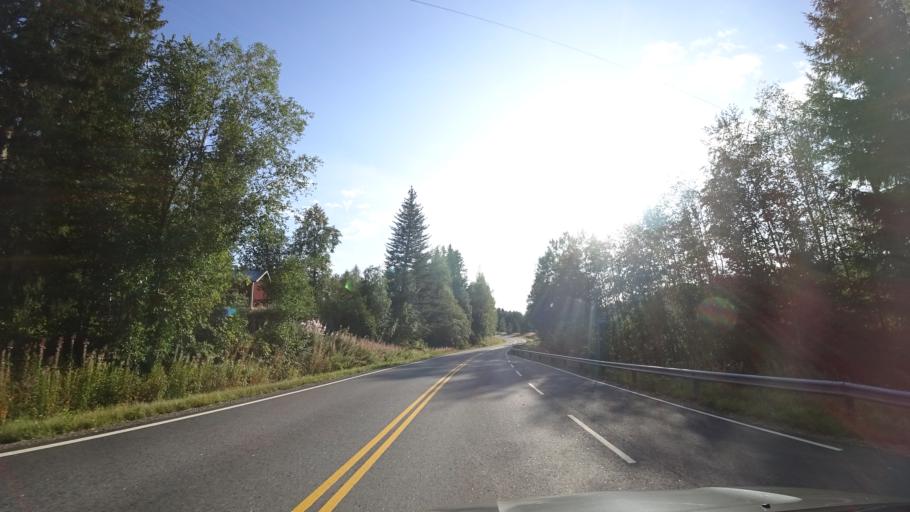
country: FI
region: Paijanne Tavastia
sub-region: Lahti
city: Hollola
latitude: 61.1390
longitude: 25.3190
